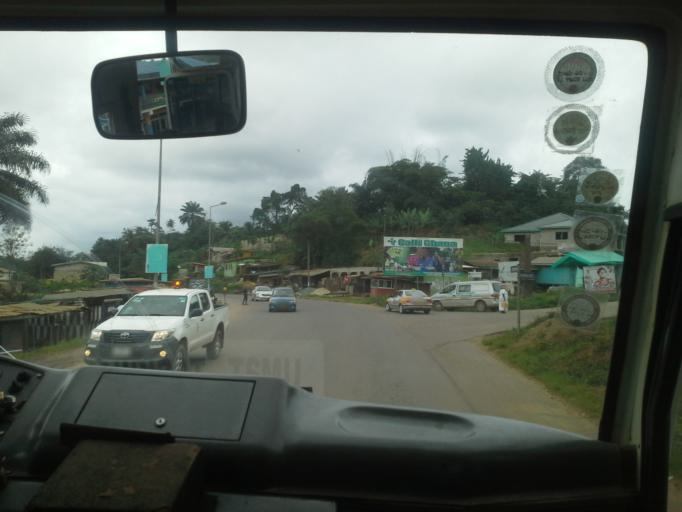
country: GH
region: Western
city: Tarkwa
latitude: 5.3126
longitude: -1.9913
